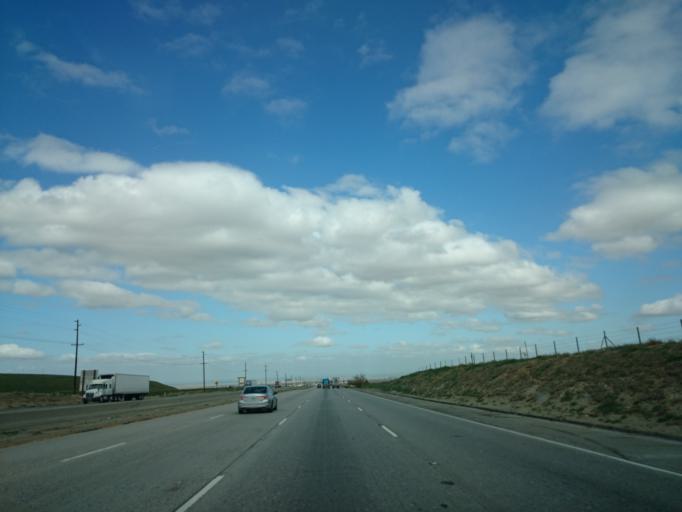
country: US
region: California
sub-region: Kern County
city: Frazier Park
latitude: 34.9954
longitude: -118.9480
